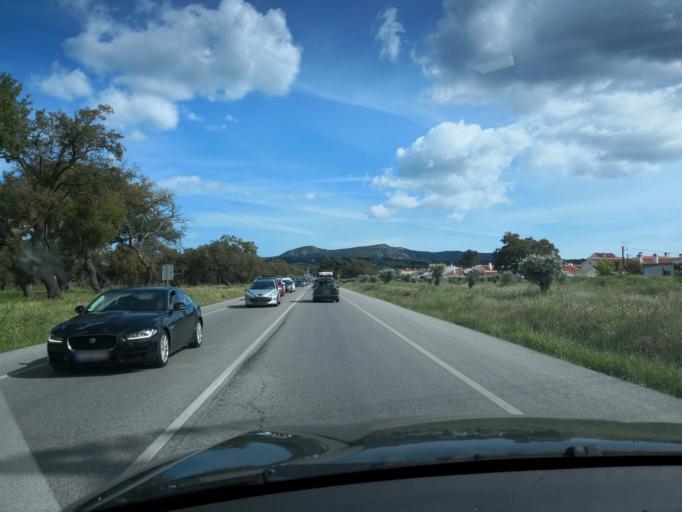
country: PT
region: Setubal
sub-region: Palmela
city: Quinta do Anjo
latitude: 38.5281
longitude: -9.0194
